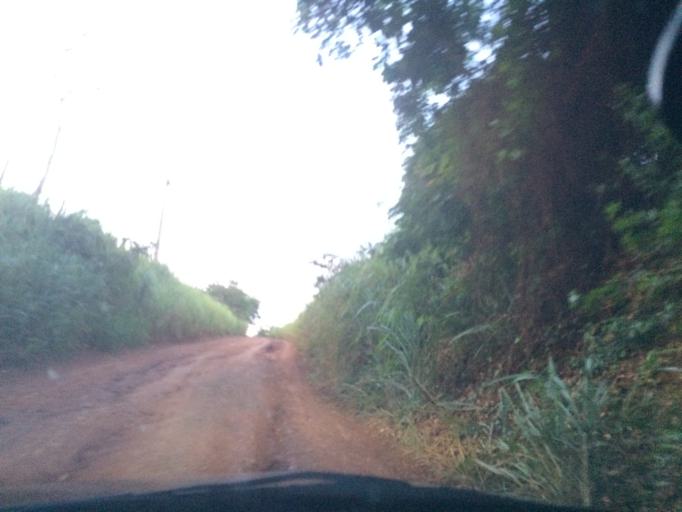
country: BR
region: Sao Paulo
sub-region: Tambau
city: Tambau
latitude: -21.7032
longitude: -47.2112
